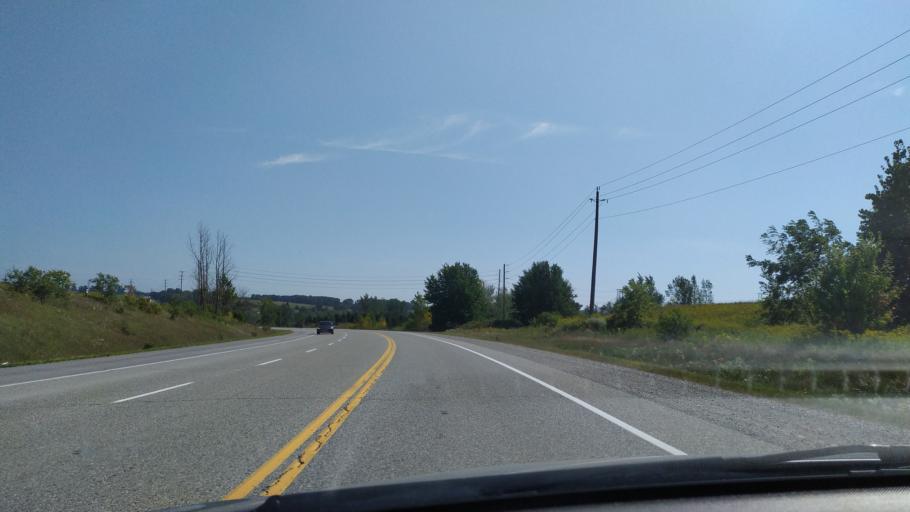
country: CA
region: Ontario
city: Ingersoll
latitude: 43.0748
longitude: -80.8595
